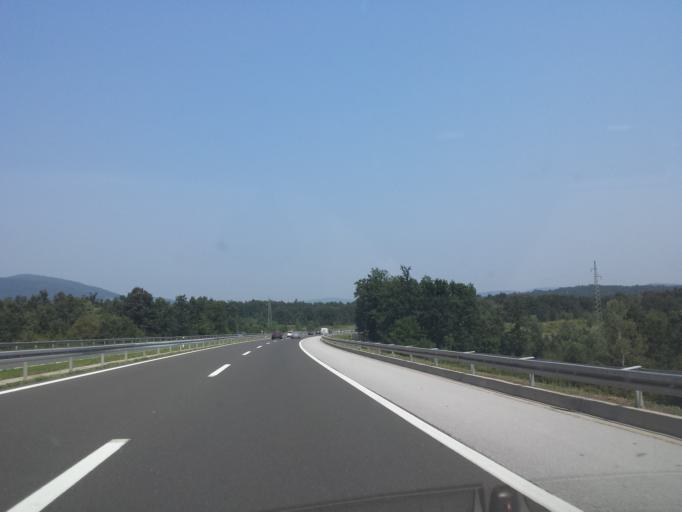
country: HR
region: Karlovacka
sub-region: Grad Ogulin
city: Ogulin
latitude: 45.2872
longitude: 15.2744
